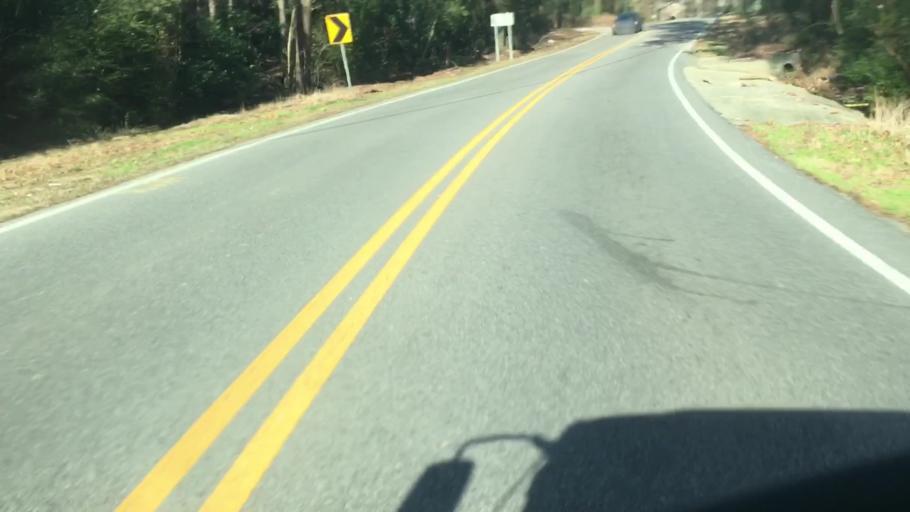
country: US
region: Alabama
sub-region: Shelby County
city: Meadowbrook
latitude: 33.4162
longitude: -86.7401
